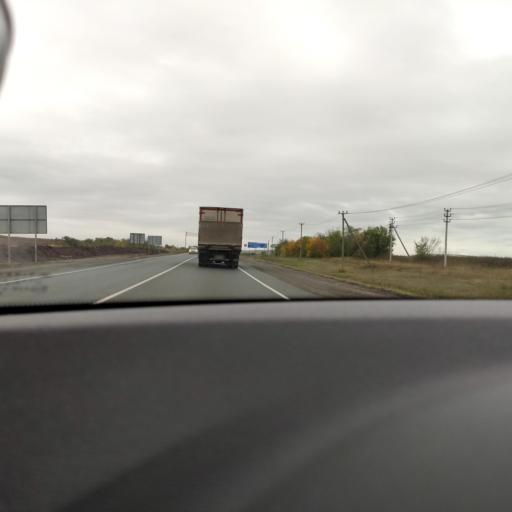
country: RU
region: Samara
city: Novosemeykino
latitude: 53.4231
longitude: 50.3549
